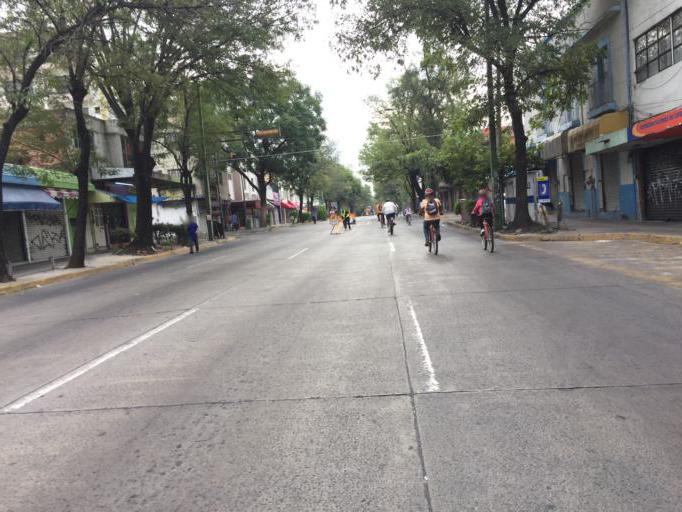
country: MX
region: Jalisco
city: Tlaquepaque
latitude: 20.6743
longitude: -103.3371
